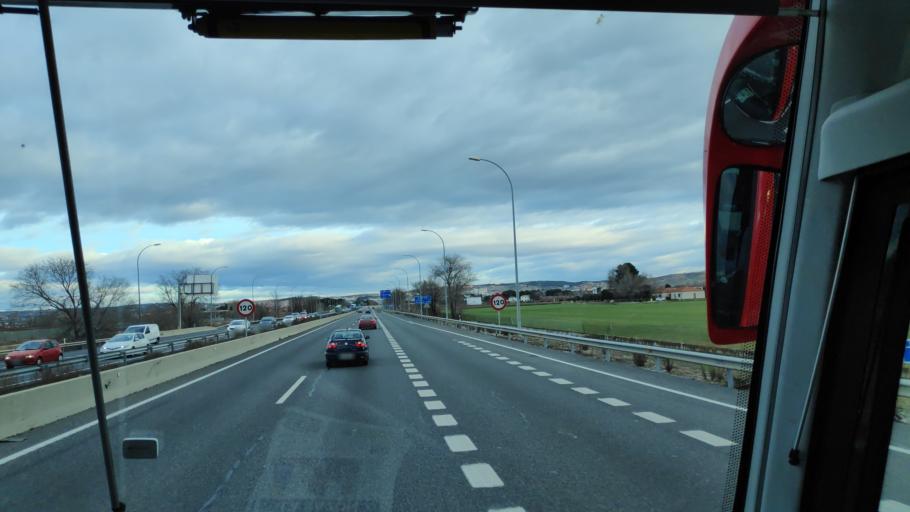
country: ES
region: Madrid
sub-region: Provincia de Madrid
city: Vaciamadrid
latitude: 40.3157
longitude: -3.5048
